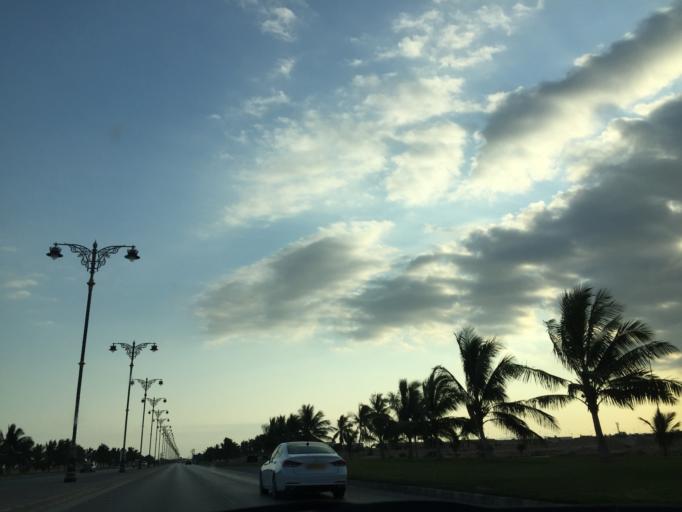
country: OM
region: Zufar
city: Salalah
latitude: 17.0451
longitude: 54.0619
